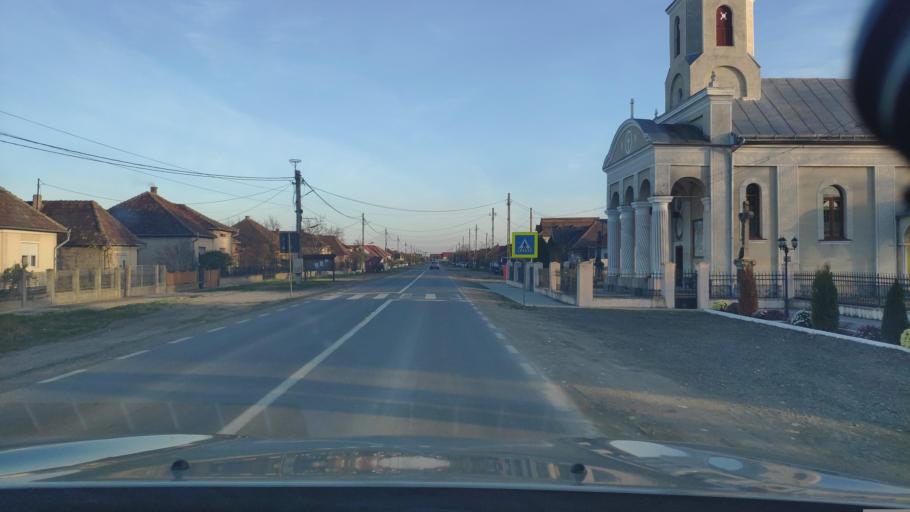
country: RO
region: Satu Mare
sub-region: Comuna Mediesu Aurit
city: Potau
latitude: 47.7768
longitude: 23.0944
